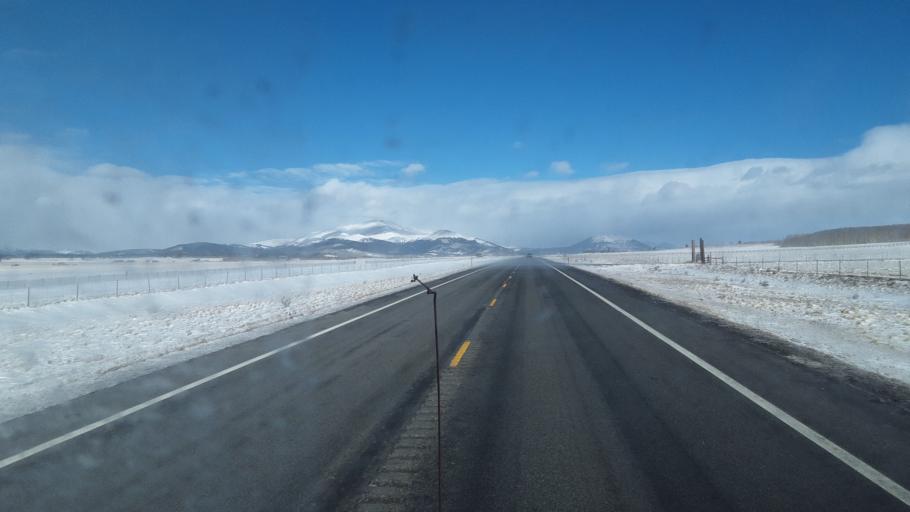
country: US
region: Colorado
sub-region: Park County
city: Fairplay
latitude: 39.1830
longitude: -105.9990
